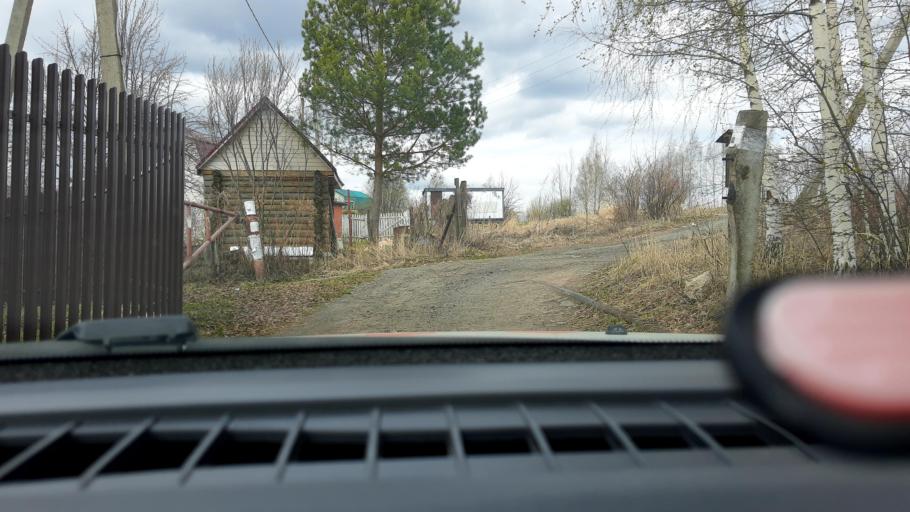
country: RU
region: Nizjnij Novgorod
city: Babino
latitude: 56.1701
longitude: 43.6755
